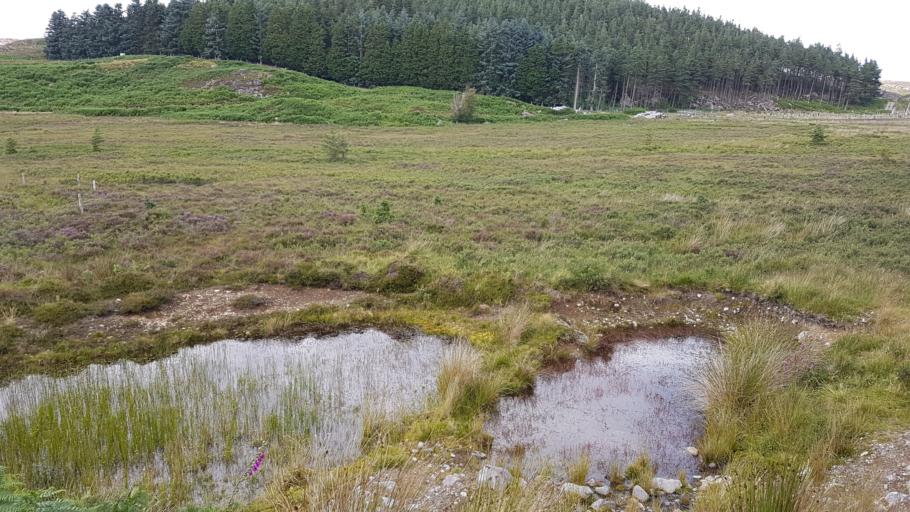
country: GB
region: Scotland
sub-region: Highland
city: Beauly
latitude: 57.2112
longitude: -4.5187
